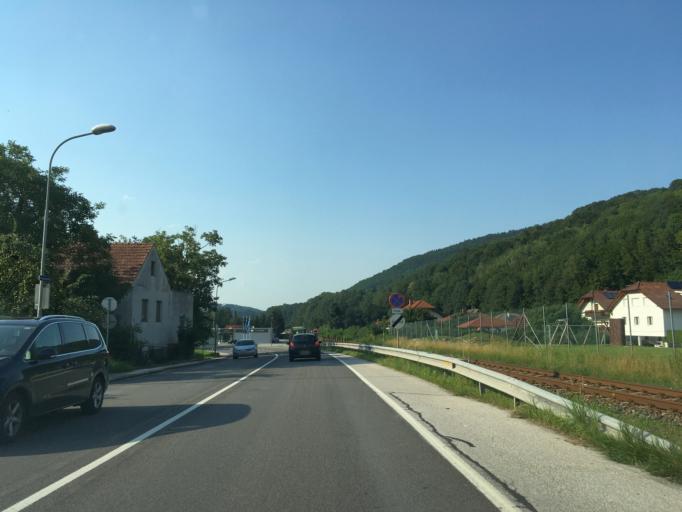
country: AT
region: Lower Austria
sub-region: Politischer Bezirk Neunkirchen
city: Grimmenstein
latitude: 47.6345
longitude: 16.1321
